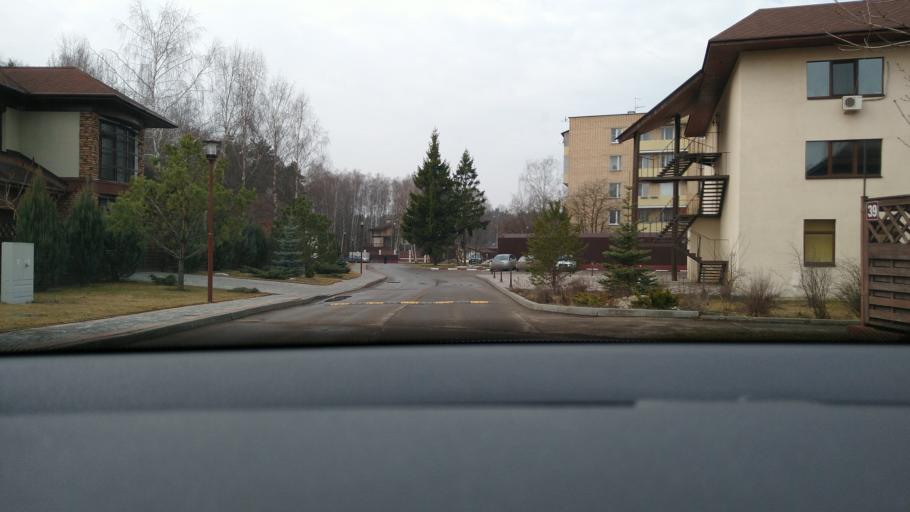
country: RU
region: Moskovskaya
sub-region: Leninskiy Rayon
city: Vnukovo
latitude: 55.6347
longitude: 37.3100
